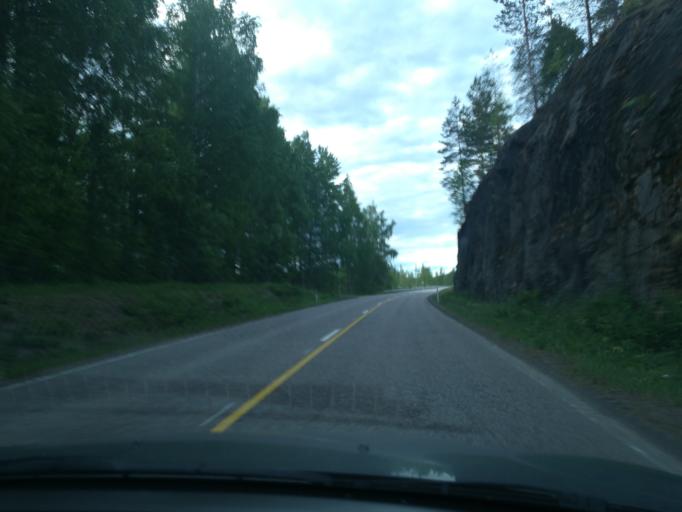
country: FI
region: Southern Savonia
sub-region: Mikkeli
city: Puumala
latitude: 61.5454
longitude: 27.9601
